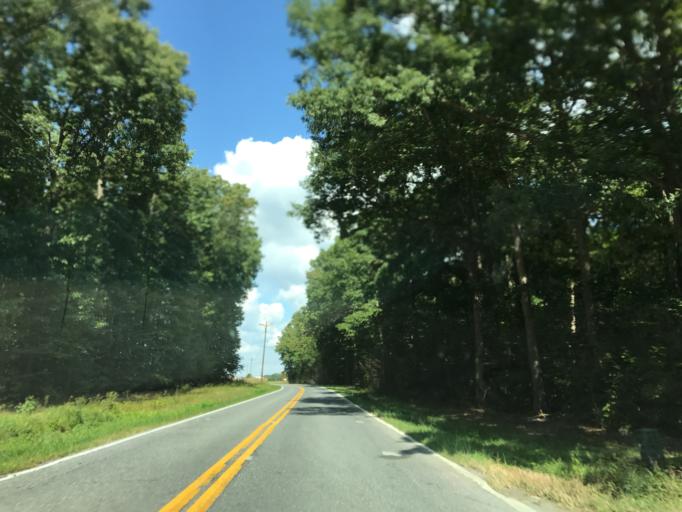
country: US
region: Maryland
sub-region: Caroline County
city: Ridgely
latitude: 39.0592
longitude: -75.9229
